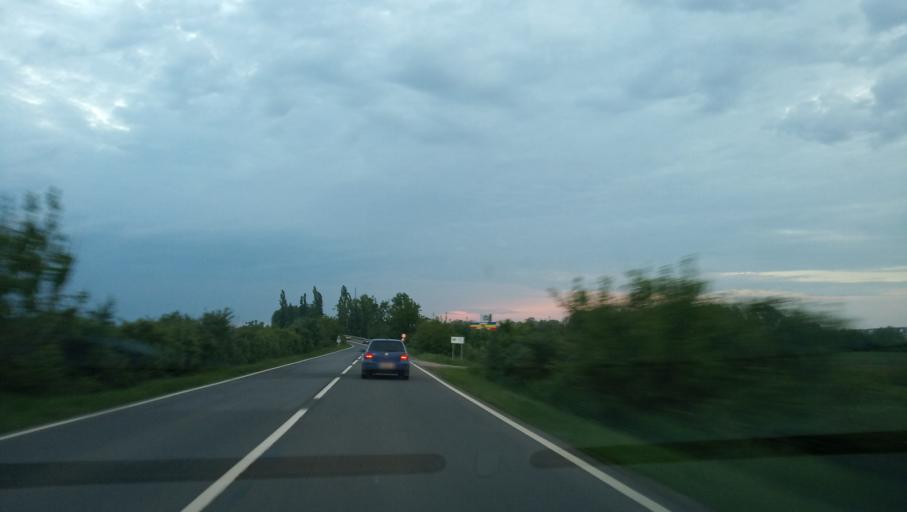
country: RO
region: Timis
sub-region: Comuna Sag
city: Sag
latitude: 45.6347
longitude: 21.1862
